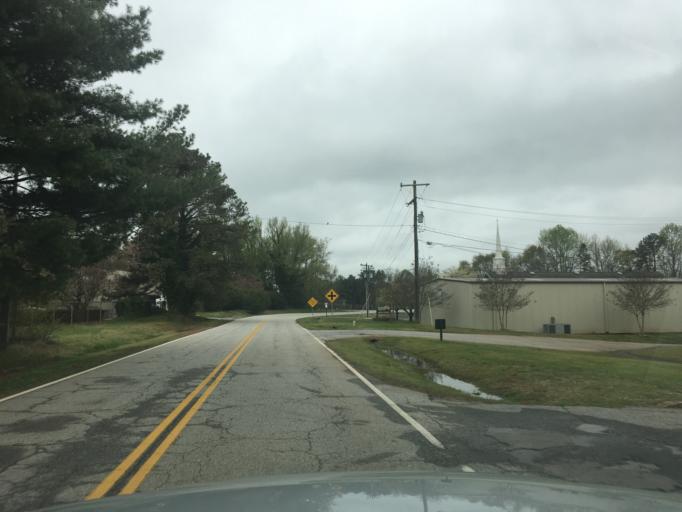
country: US
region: South Carolina
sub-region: Spartanburg County
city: Southern Shops
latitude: 34.9725
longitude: -82.0045
